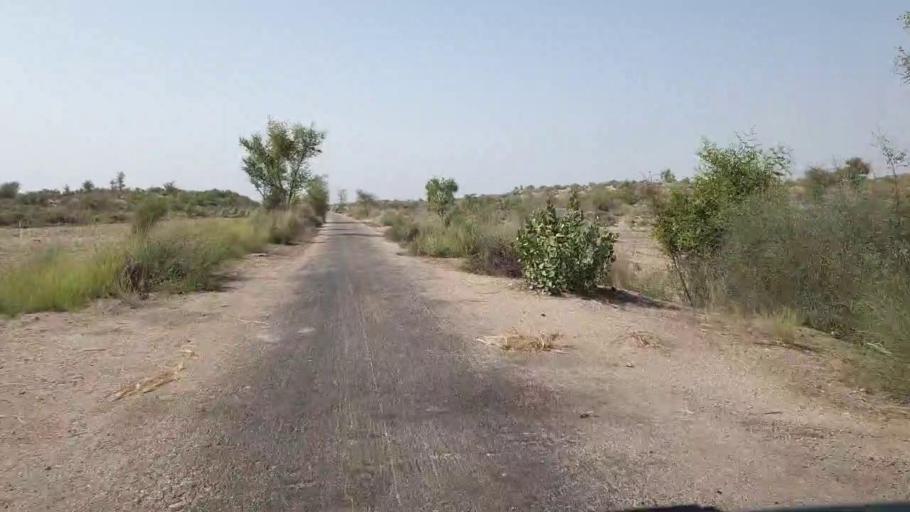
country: PK
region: Sindh
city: Jam Sahib
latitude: 26.5679
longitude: 68.9225
